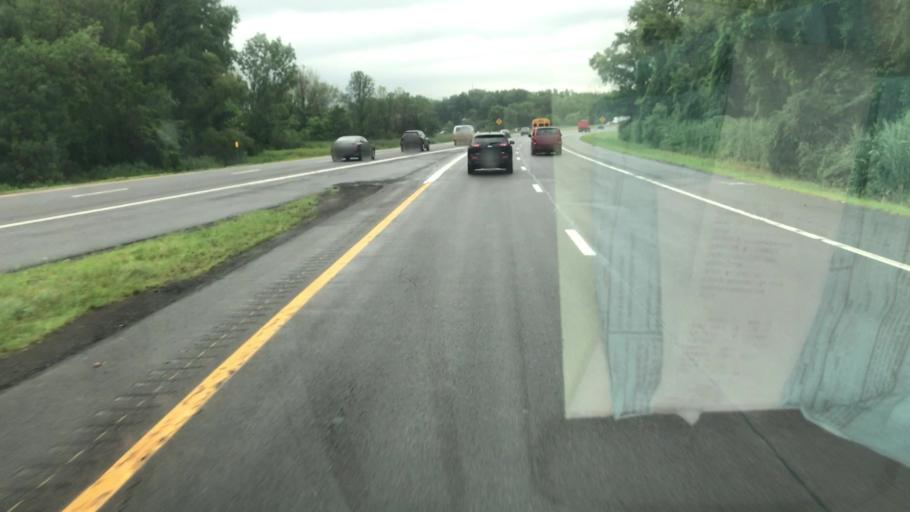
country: US
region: New York
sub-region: Onondaga County
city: East Syracuse
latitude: 43.0502
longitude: -76.0528
